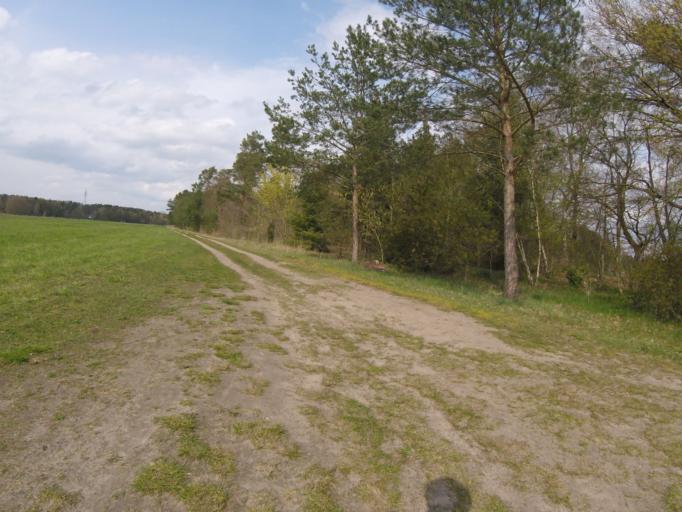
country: DE
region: Brandenburg
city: Bestensee
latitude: 52.2295
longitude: 13.6044
